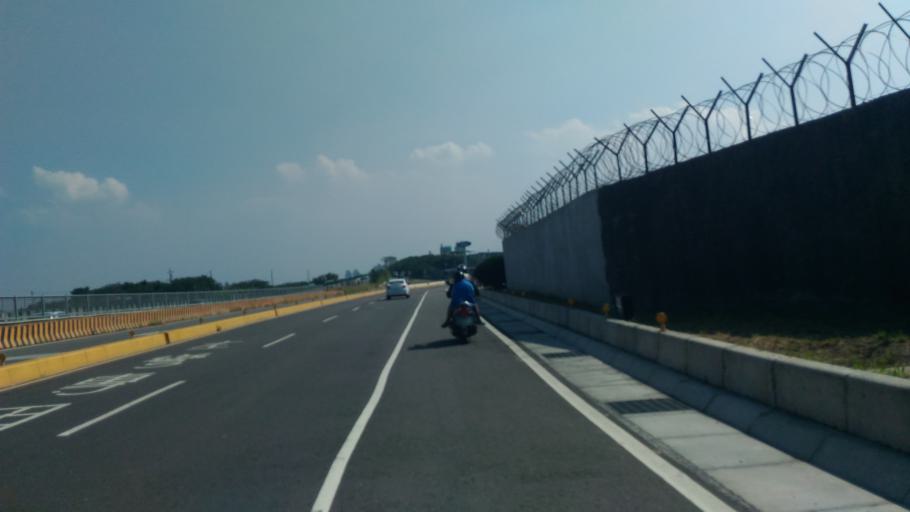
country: TW
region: Taiwan
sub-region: Hsinchu
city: Hsinchu
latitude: 24.8323
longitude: 120.9537
